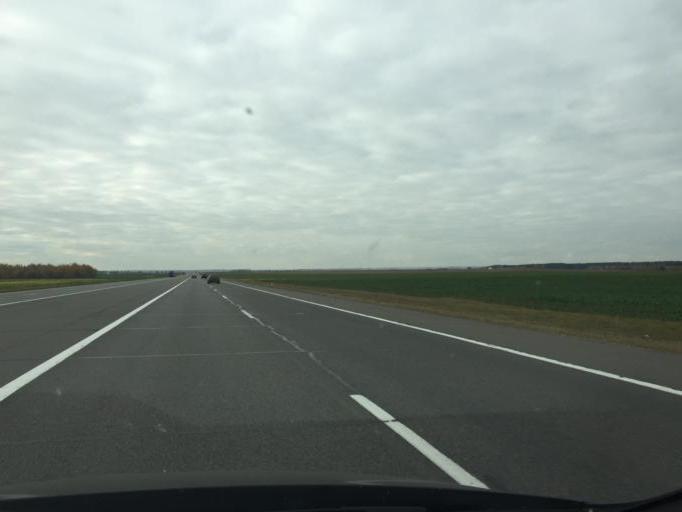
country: BY
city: Fanipol
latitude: 53.6851
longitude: 27.3146
